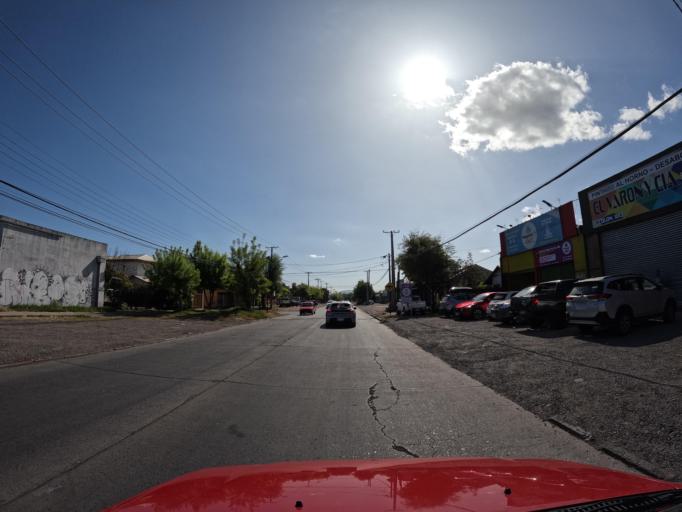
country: CL
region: Maule
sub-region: Provincia de Curico
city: Curico
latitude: -34.9761
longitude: -71.2498
